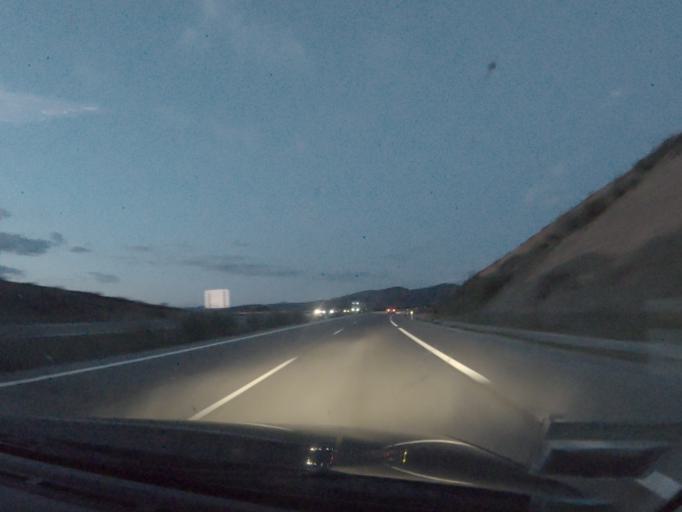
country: ES
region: Castille and Leon
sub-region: Provincia de Leon
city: Folgoso de la Ribera
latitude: 42.6203
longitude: -6.3237
